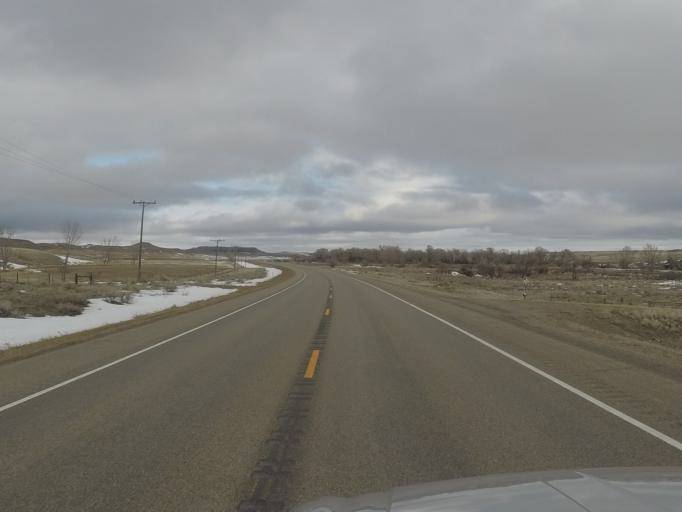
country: US
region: Montana
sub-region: Golden Valley County
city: Ryegate
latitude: 46.3194
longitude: -109.4335
